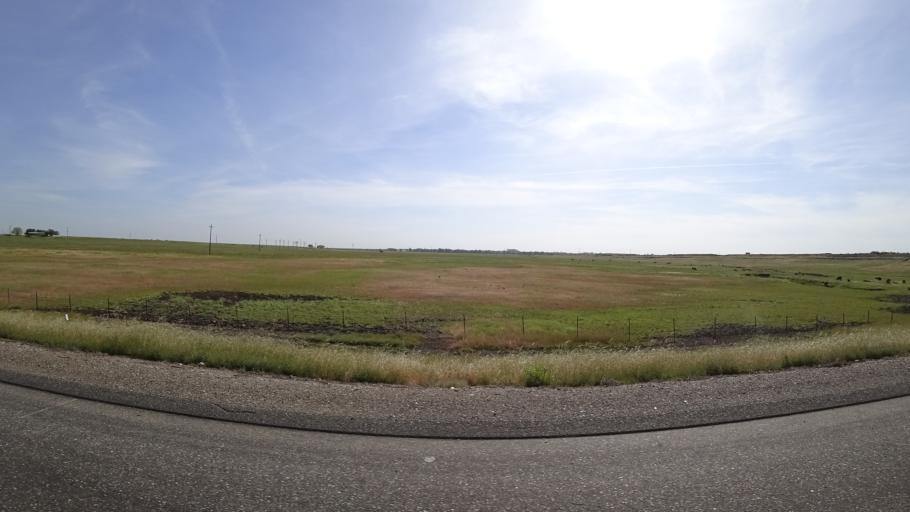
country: US
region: California
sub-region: Butte County
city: Durham
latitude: 39.6575
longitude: -121.7338
